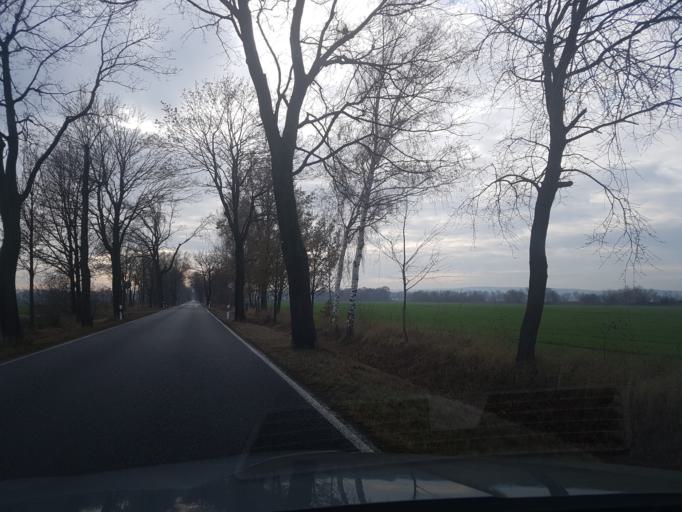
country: DE
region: Brandenburg
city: Hirschfeld
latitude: 51.4221
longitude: 13.6228
